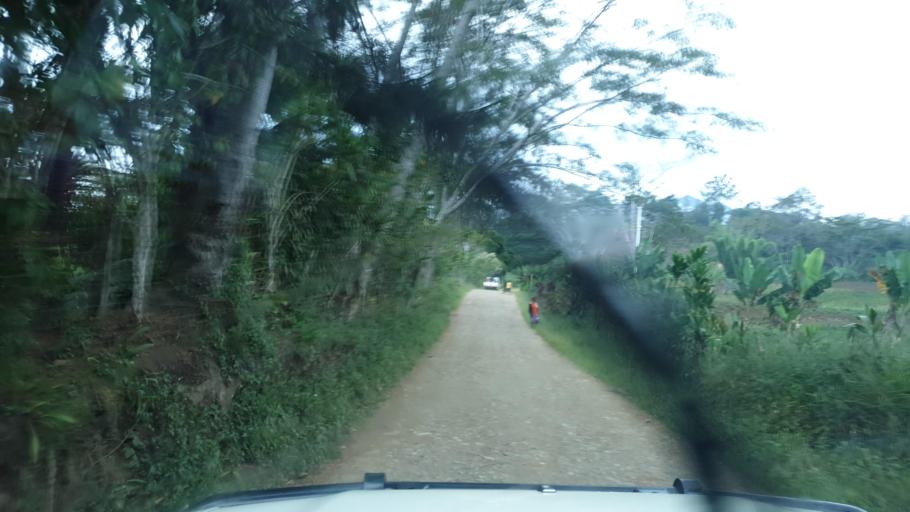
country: PG
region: Eastern Highlands
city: Goroka
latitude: -5.9846
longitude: 145.2828
